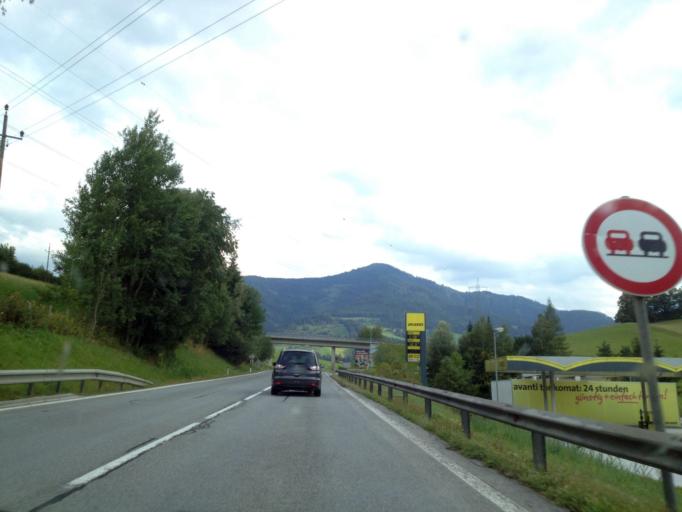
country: AT
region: Styria
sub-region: Politischer Bezirk Liezen
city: Grobming
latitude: 47.4471
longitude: 13.9129
